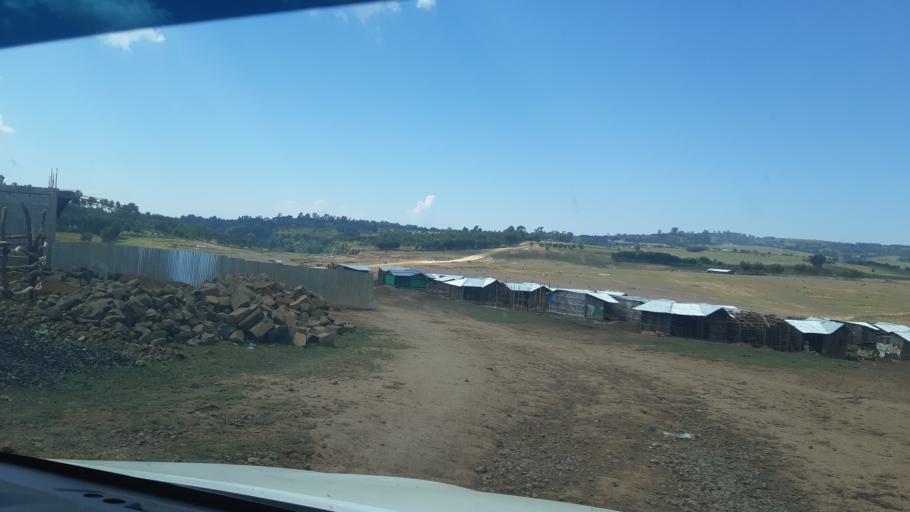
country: ET
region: Amhara
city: Dabat
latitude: 13.3899
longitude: 37.3995
